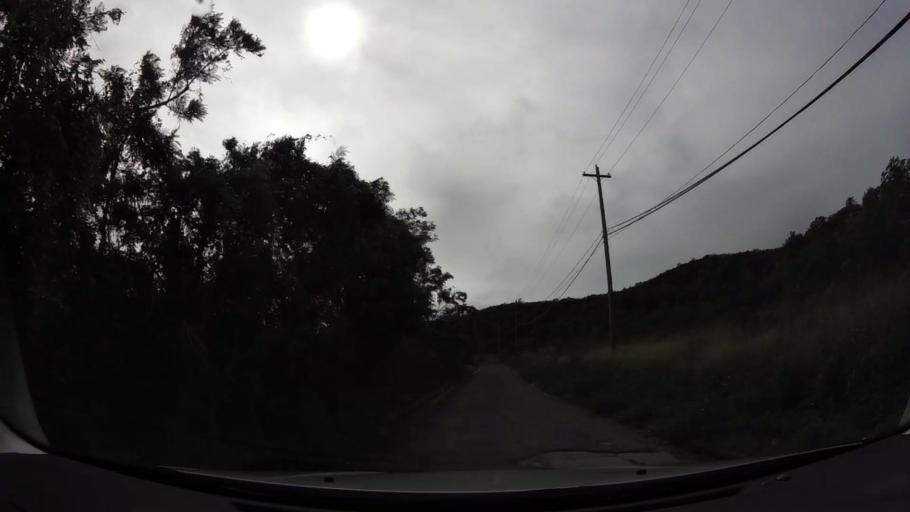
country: AG
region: Saint Peter
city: Parham
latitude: 17.0639
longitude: -61.7259
